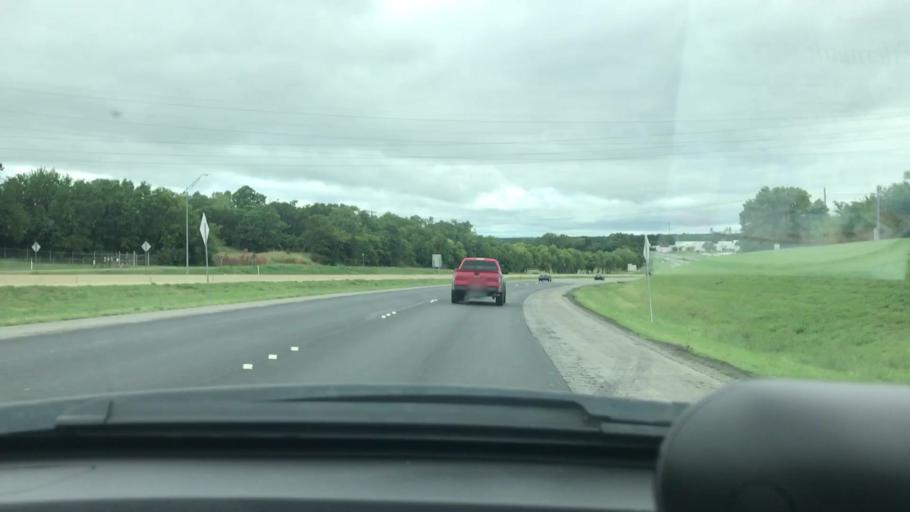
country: US
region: Texas
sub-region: Grayson County
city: Sherman
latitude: 33.6047
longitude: -96.6097
